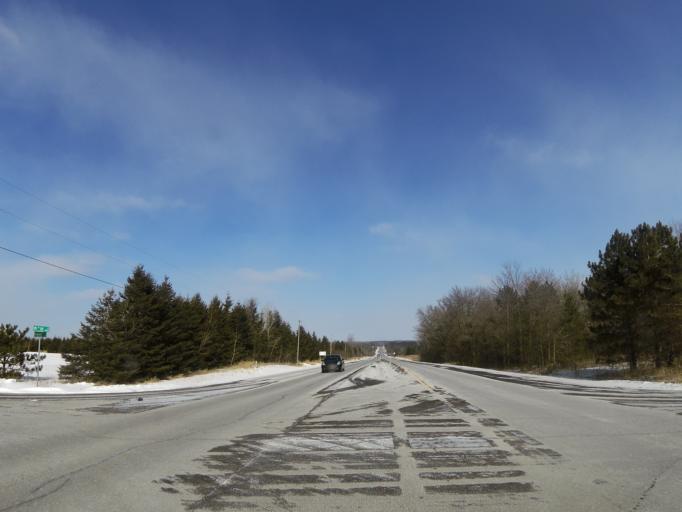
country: US
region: Minnesota
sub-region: Washington County
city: Oakdale
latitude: 44.9706
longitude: -92.9338
